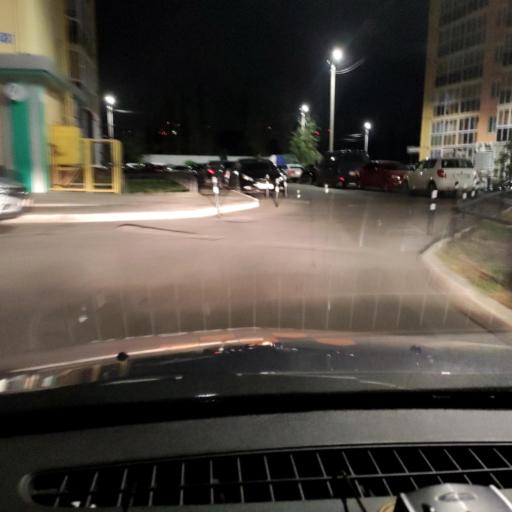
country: RU
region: Voronezj
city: Voronezh
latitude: 51.7028
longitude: 39.2001
